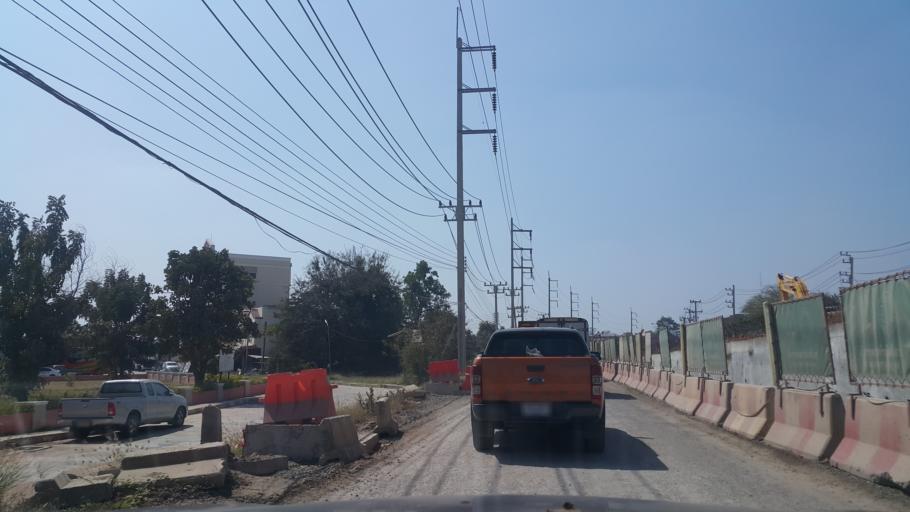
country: TH
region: Nakhon Ratchasima
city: Bua Yai
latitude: 15.5925
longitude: 102.4282
